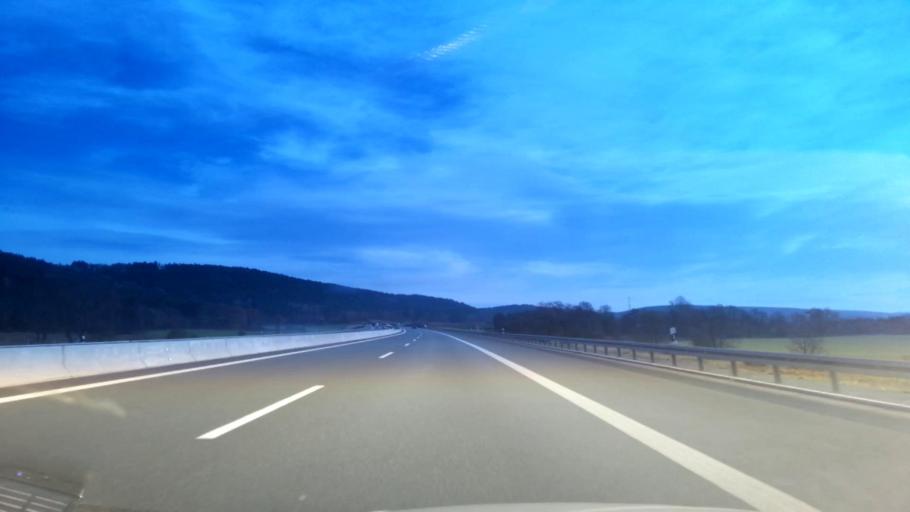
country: DE
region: Bavaria
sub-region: Upper Franconia
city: Harsdorf
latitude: 50.0337
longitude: 11.5492
